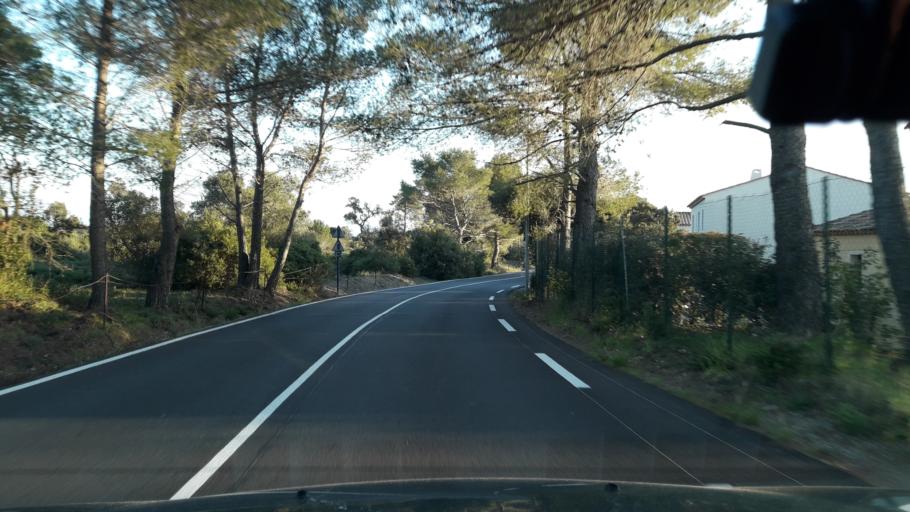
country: FR
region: Provence-Alpes-Cote d'Azur
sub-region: Departement du Var
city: Saint-Raphael
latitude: 43.4675
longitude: 6.7664
